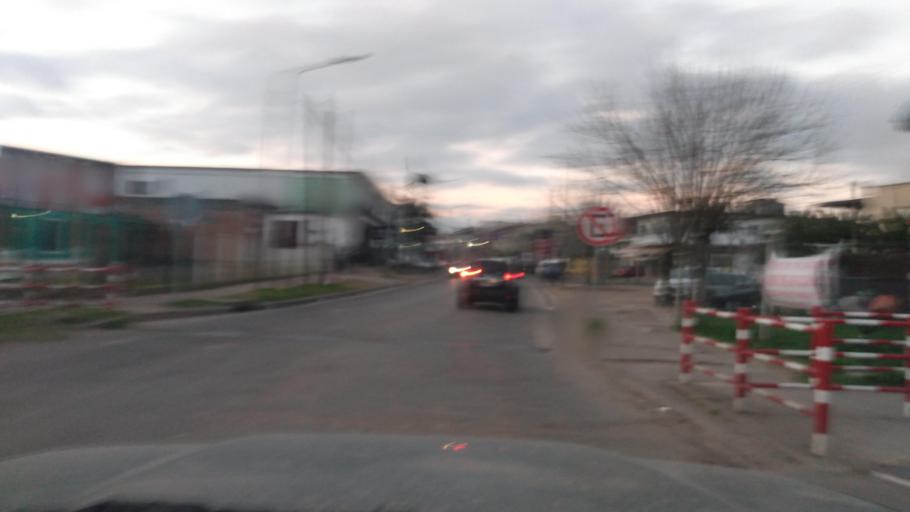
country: AR
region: Buenos Aires
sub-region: Partido de Pilar
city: Pilar
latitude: -34.4664
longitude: -58.9153
